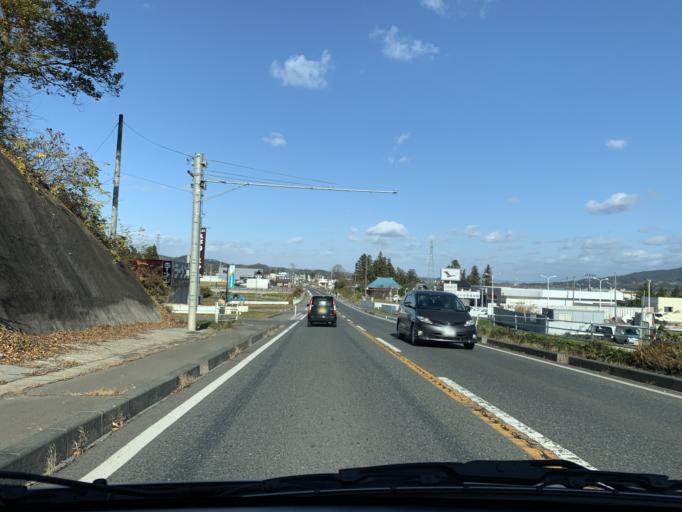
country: JP
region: Iwate
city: Ichinoseki
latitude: 38.9610
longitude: 141.1216
